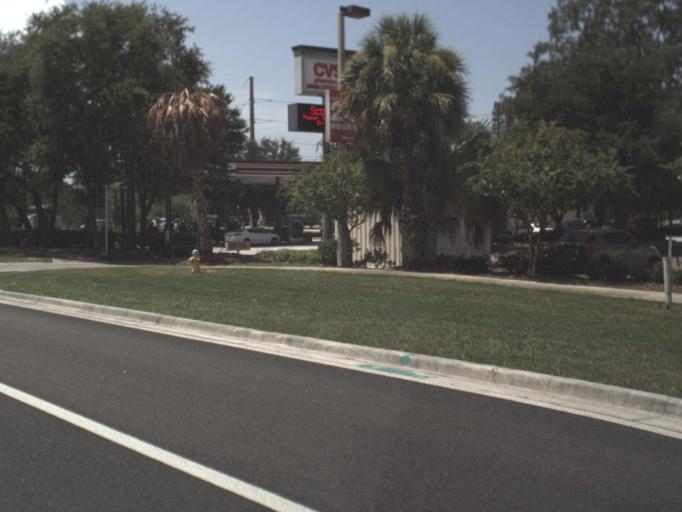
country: US
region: Florida
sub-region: Hillsborough County
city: Riverview
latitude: 27.8564
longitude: -82.3268
